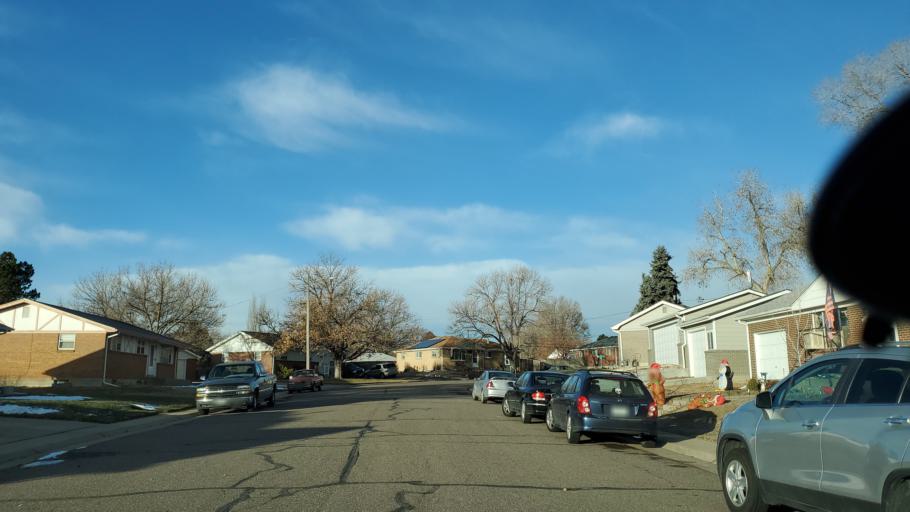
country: US
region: Colorado
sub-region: Adams County
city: Northglenn
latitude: 39.9029
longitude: -104.9626
